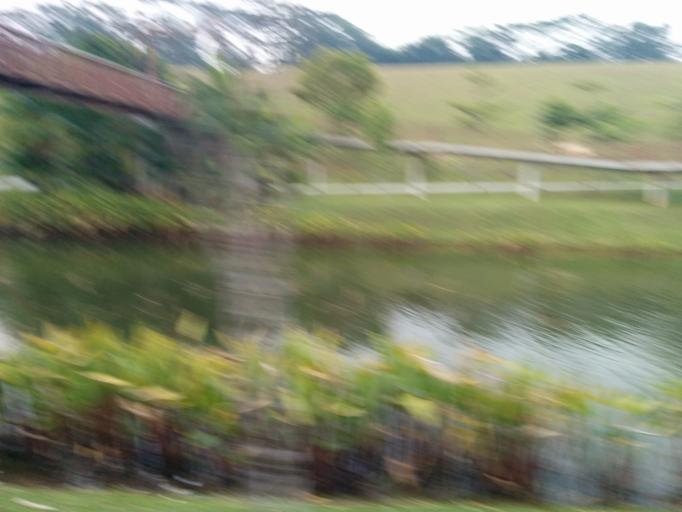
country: MY
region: Johor
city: Kampung Pasir Gudang Baru
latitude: 1.4117
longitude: 103.9042
